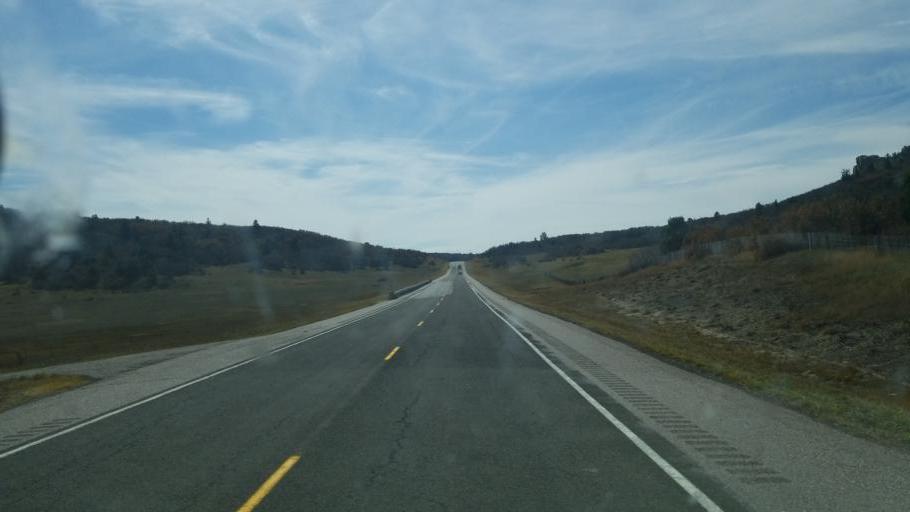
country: US
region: New Mexico
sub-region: Rio Arriba County
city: Chama
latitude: 36.9783
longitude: -106.7803
